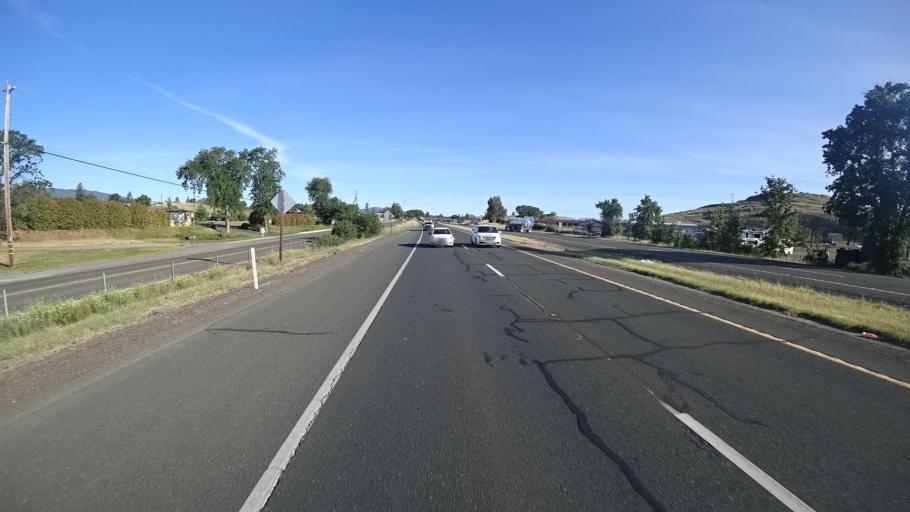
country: US
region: California
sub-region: Lake County
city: Lakeport
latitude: 39.0284
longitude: -122.9209
